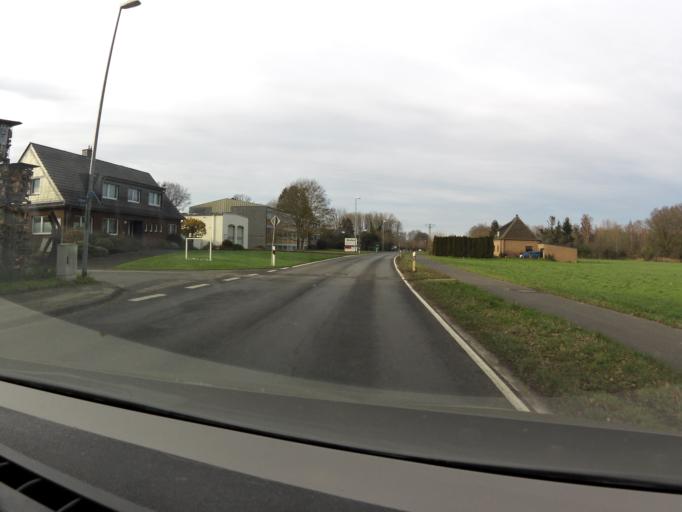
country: DE
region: North Rhine-Westphalia
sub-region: Regierungsbezirk Dusseldorf
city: Nettetal
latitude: 51.3067
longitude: 6.2449
